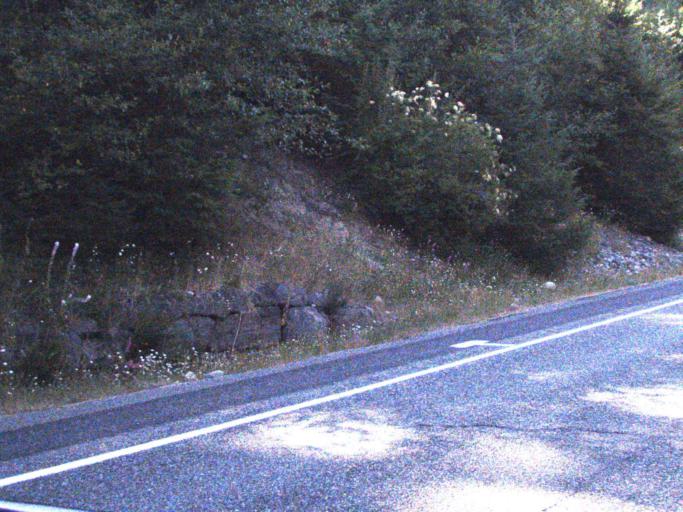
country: US
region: Washington
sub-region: King County
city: Enumclaw
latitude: 47.0639
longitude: -121.5758
